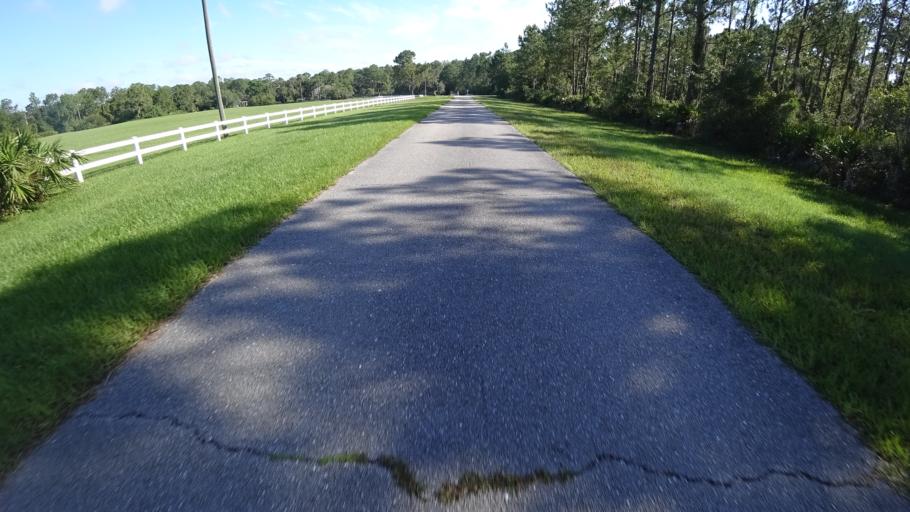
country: US
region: Florida
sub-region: Sarasota County
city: The Meadows
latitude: 27.4178
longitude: -82.3404
